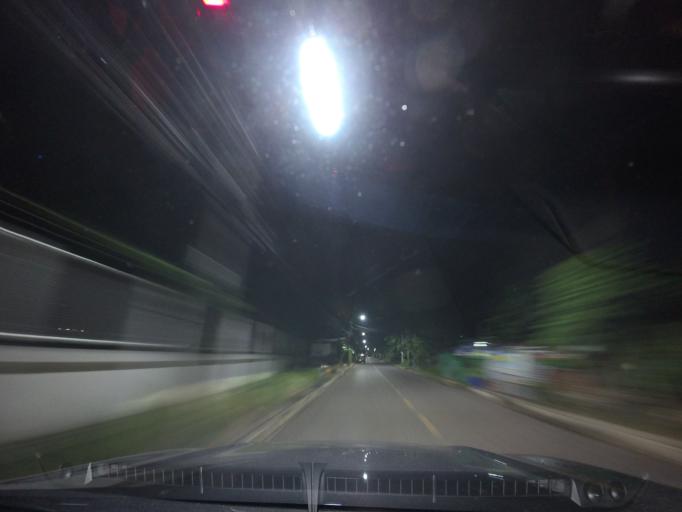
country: TH
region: Nong Khai
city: Nong Khai
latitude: 17.8691
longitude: 102.7172
